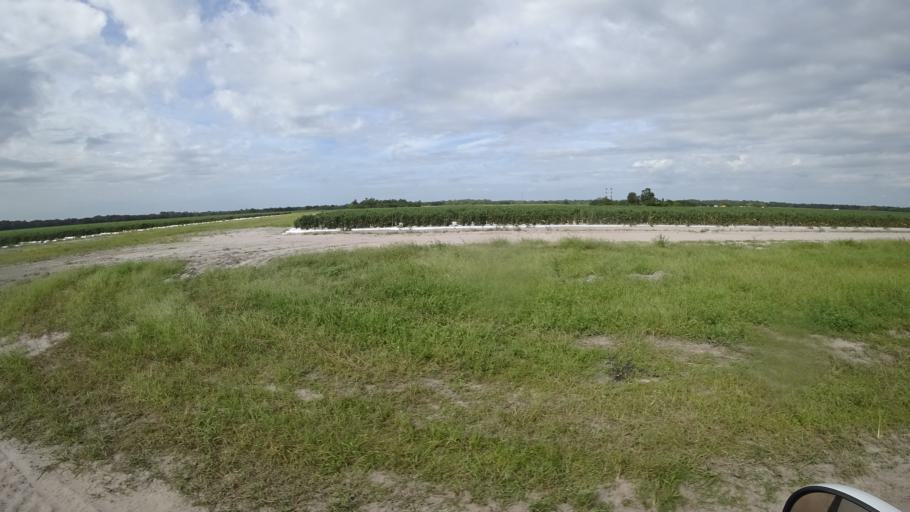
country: US
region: Florida
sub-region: Hillsborough County
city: Wimauma
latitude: 27.5850
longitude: -82.3136
